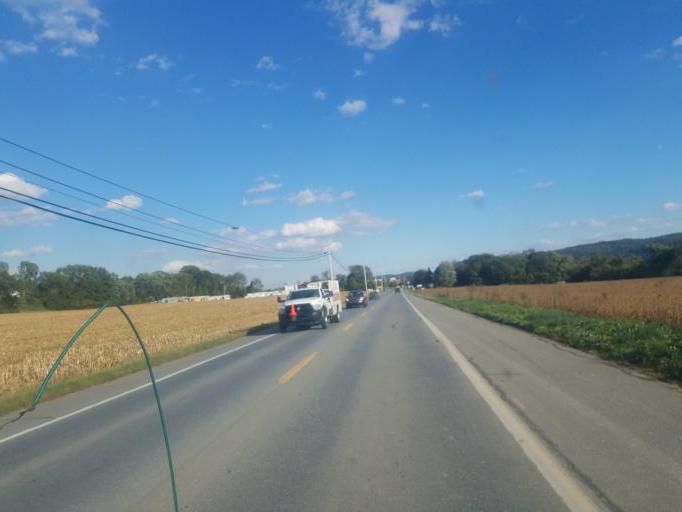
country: US
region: Pennsylvania
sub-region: Lancaster County
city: Maytown
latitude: 40.0620
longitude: -76.5748
